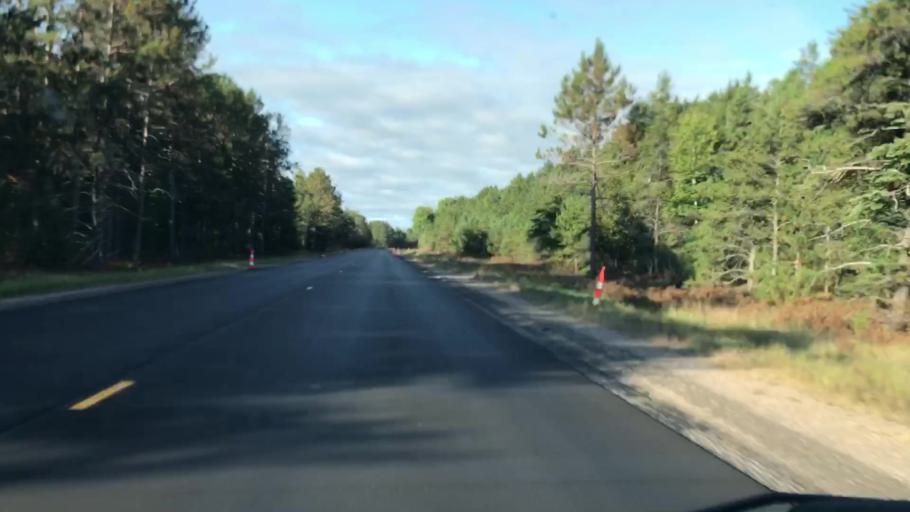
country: US
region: Michigan
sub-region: Mackinac County
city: Saint Ignace
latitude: 46.3492
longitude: -84.9118
